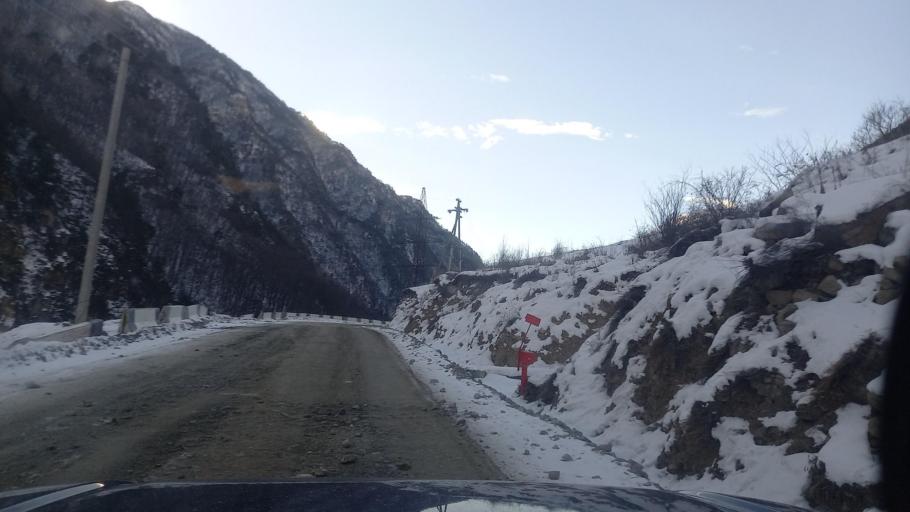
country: RU
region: North Ossetia
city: Chikola
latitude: 42.9800
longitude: 43.7690
